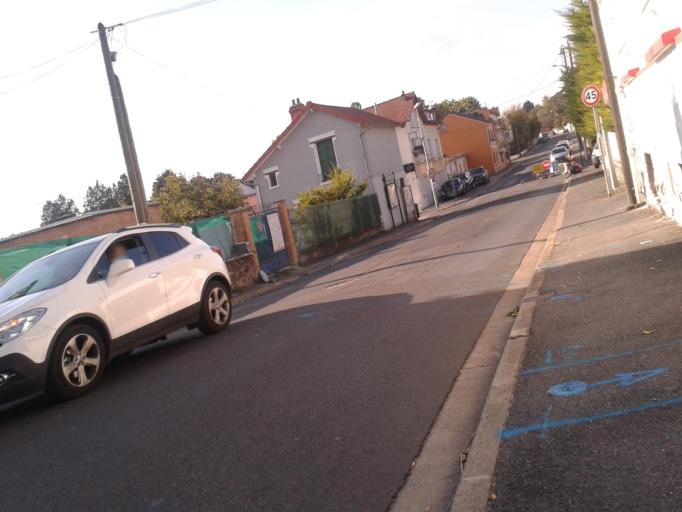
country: FR
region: Ile-de-France
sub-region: Departement du Val-d'Oise
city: La Frette-sur-Seine
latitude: 48.9846
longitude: 2.1817
